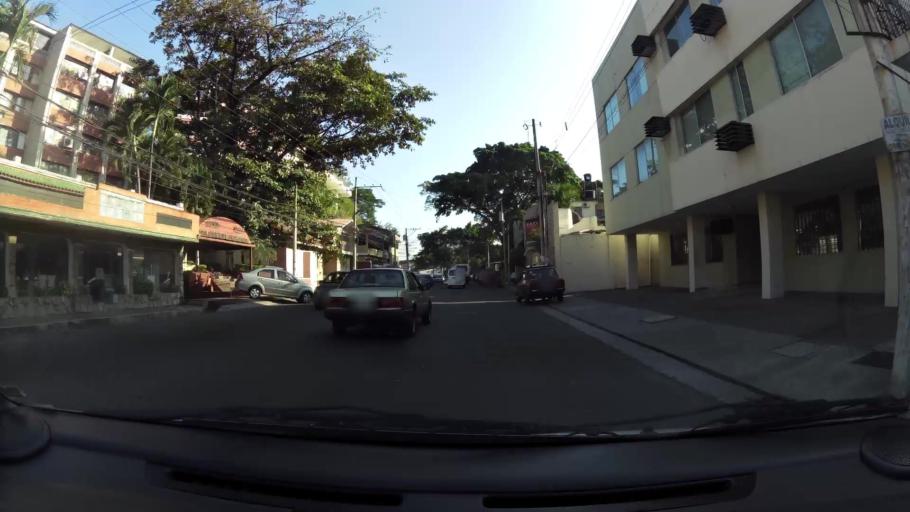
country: EC
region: Guayas
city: Guayaquil
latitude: -2.1651
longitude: -79.9019
